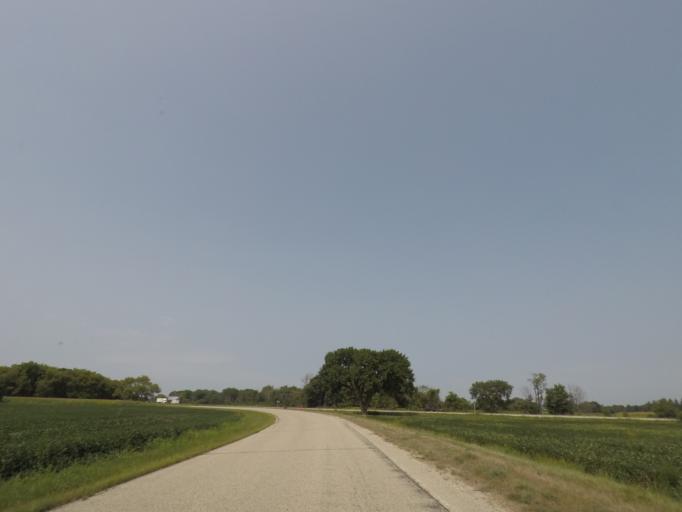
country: US
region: Wisconsin
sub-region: Jefferson County
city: Ixonia
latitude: 43.0690
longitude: -88.5731
